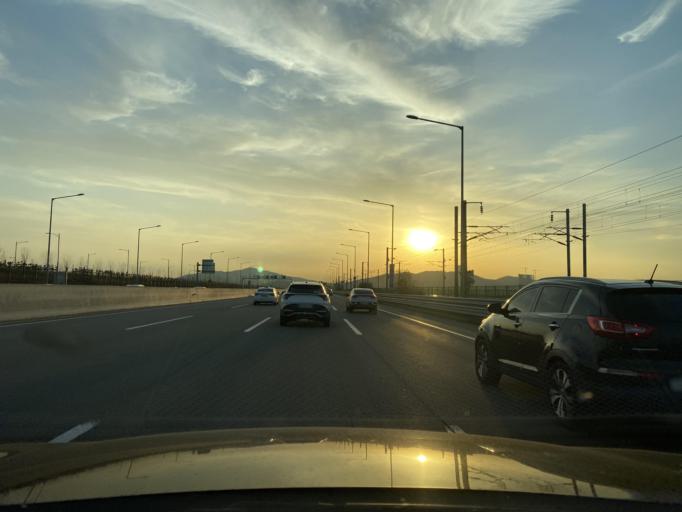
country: KR
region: Gyeonggi-do
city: Tongjin
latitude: 37.5333
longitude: 126.5571
